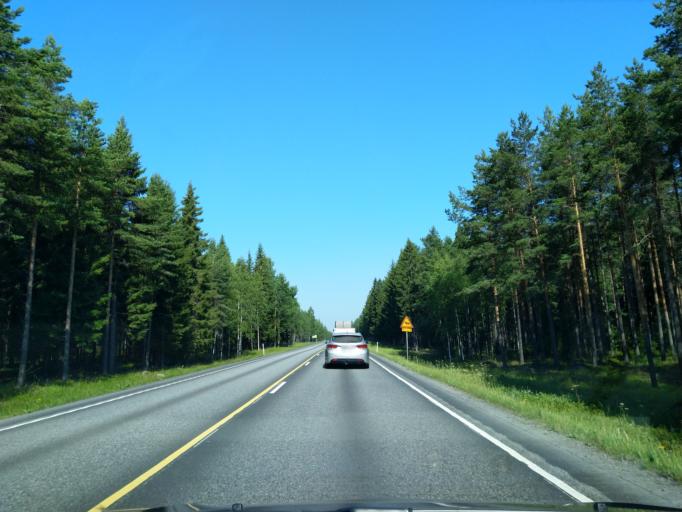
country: FI
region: Satakunta
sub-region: Pori
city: Huittinen
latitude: 61.1247
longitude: 22.8069
